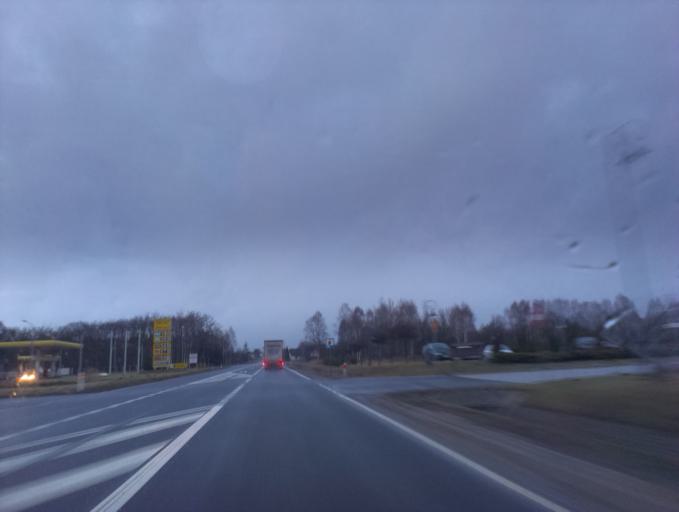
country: PL
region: Lodz Voivodeship
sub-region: Powiat opoczynski
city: Zarnow
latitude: 51.2040
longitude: 20.2019
